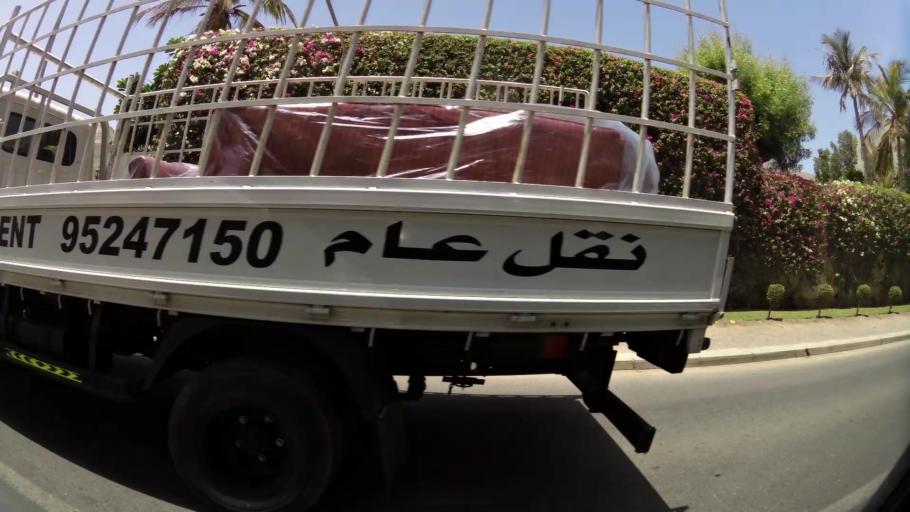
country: OM
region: Muhafazat Masqat
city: Muscat
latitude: 23.6253
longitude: 58.4978
